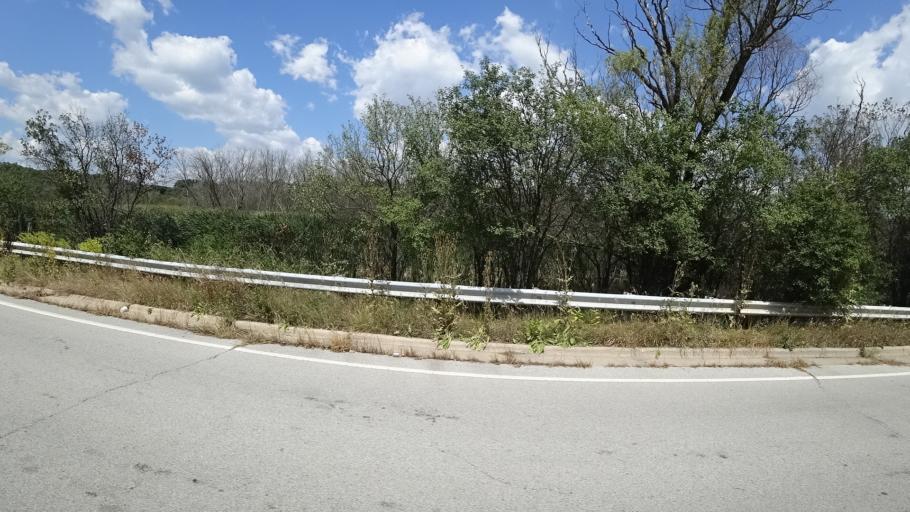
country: US
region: Illinois
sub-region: Cook County
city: Palos Heights
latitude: 41.6463
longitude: -87.7935
